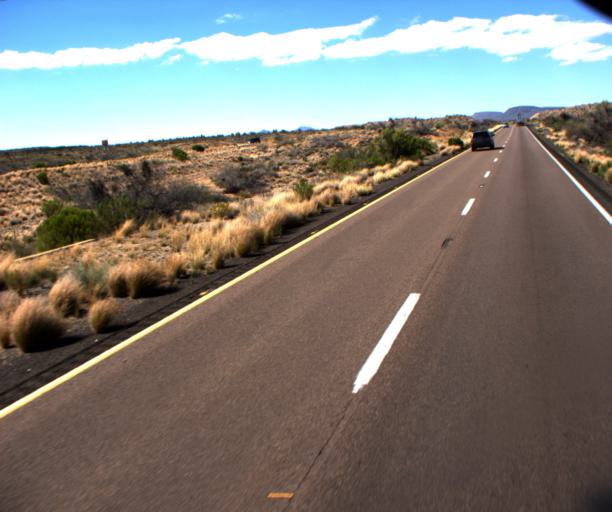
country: US
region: Arizona
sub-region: Mohave County
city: Kingman
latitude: 35.0686
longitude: -113.6651
